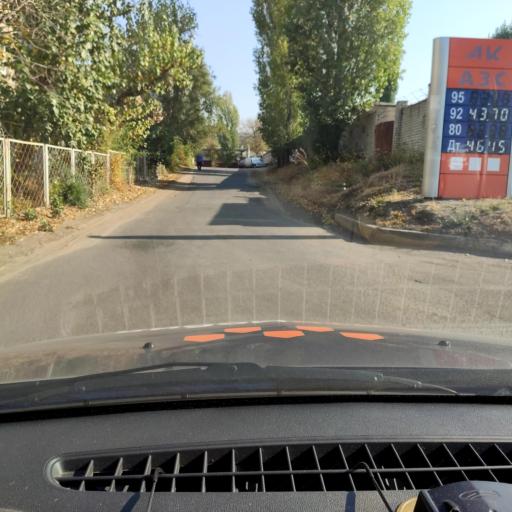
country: RU
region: Voronezj
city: Voronezh
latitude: 51.6322
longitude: 39.2401
